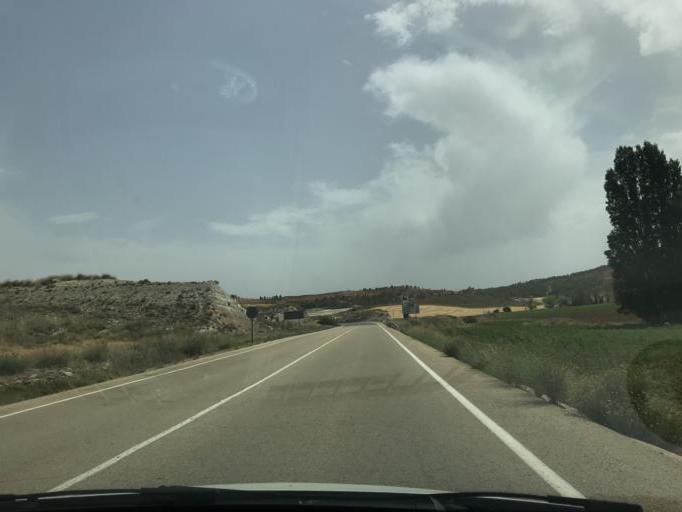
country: ES
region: Castille-La Mancha
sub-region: Provincia de Cuenca
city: Villar de Domingo Garcia
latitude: 40.2463
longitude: -2.3001
